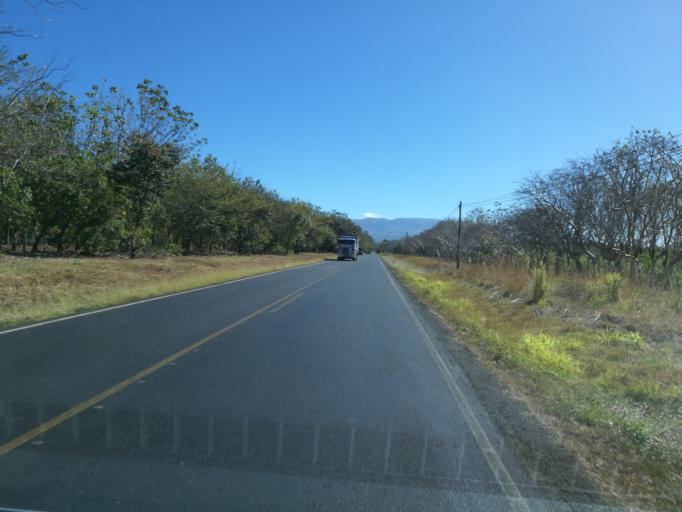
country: CR
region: Puntarenas
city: Miramar
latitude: 10.0887
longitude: -84.8329
